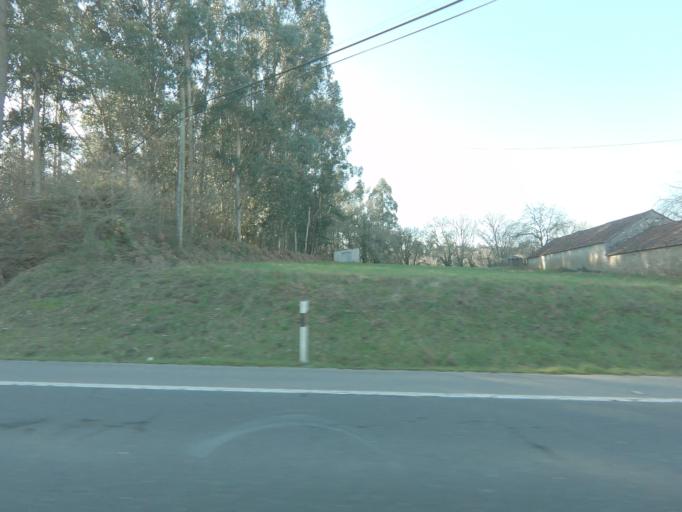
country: ES
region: Galicia
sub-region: Provincia de Pontevedra
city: Silleda
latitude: 42.7120
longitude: -8.2938
